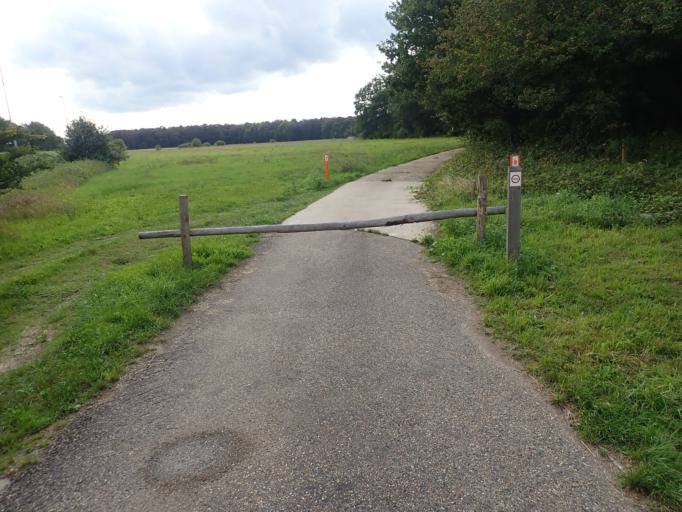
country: BE
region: Flanders
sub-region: Provincie Antwerpen
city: Zoersel
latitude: 51.2433
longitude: 4.6921
